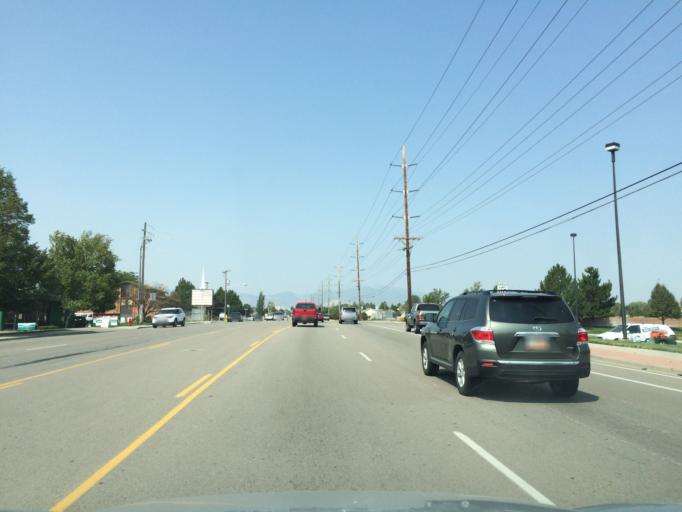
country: US
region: Utah
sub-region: Salt Lake County
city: West Jordan
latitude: 40.5877
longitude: -111.9404
